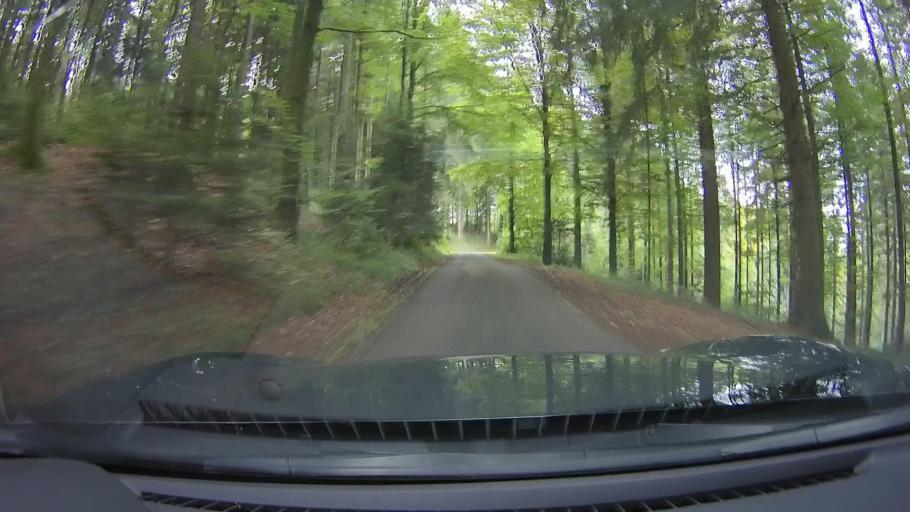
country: DE
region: Baden-Wuerttemberg
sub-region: Regierungsbezirk Stuttgart
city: Kaisersbach
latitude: 48.9483
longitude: 9.6490
